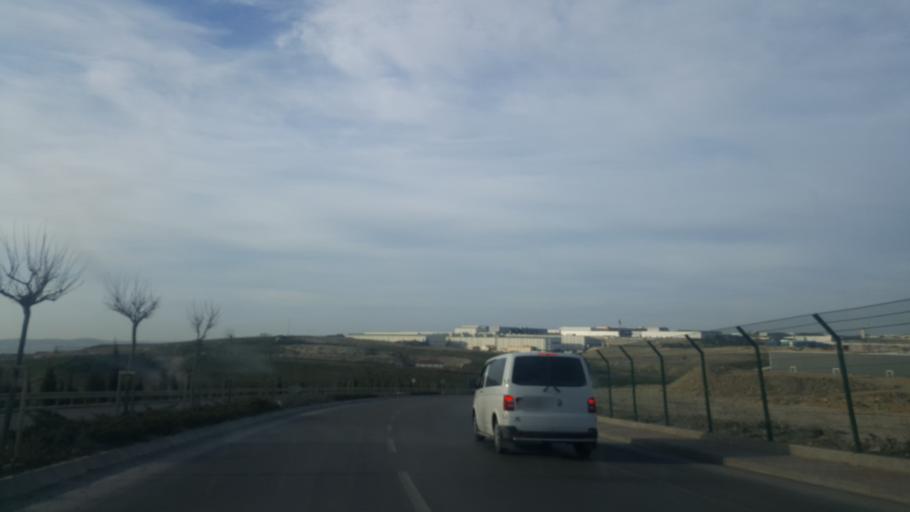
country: TR
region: Kocaeli
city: Tavsanli
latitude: 40.8228
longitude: 29.5590
